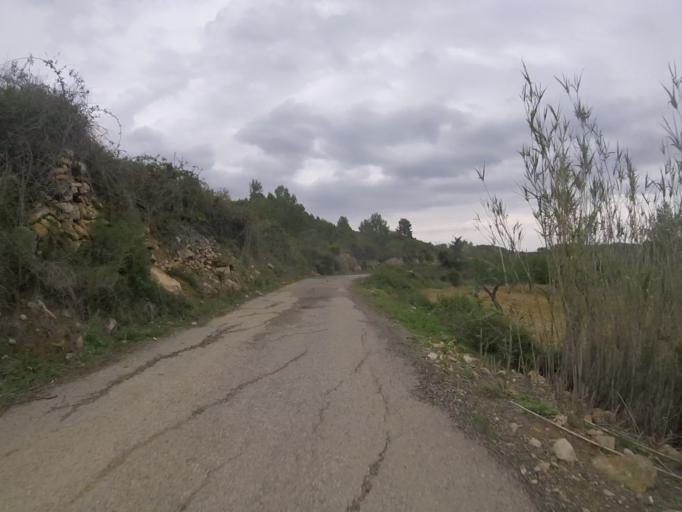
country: ES
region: Valencia
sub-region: Provincia de Castello
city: Sarratella
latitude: 40.2685
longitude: 0.0696
